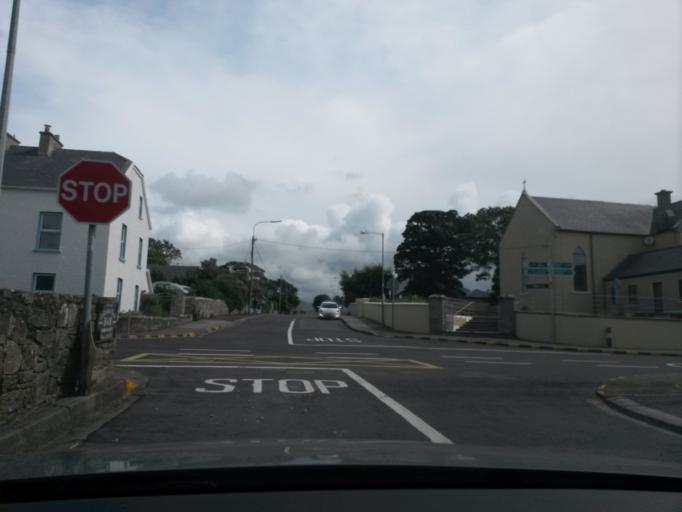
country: IE
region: Connaught
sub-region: Sligo
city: Sligo
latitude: 54.4304
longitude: -8.4541
